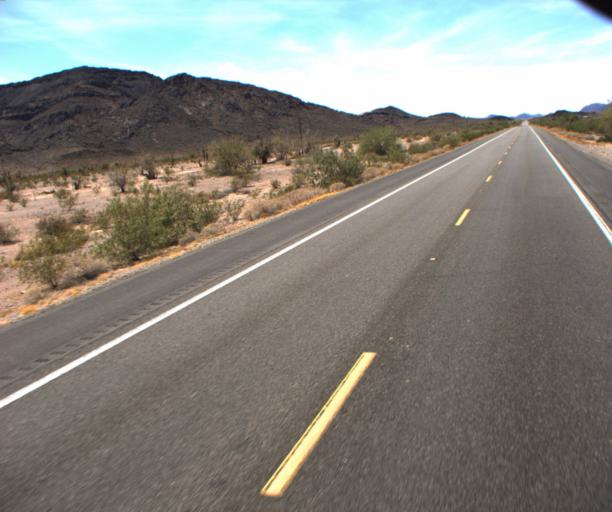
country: US
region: Arizona
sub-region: La Paz County
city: Salome
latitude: 33.6885
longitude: -113.9090
